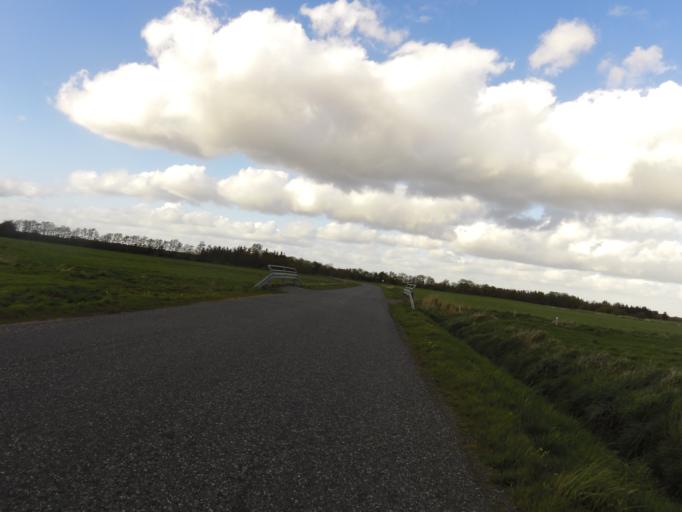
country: DK
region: South Denmark
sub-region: Esbjerg Kommune
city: Ribe
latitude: 55.3297
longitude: 8.8147
